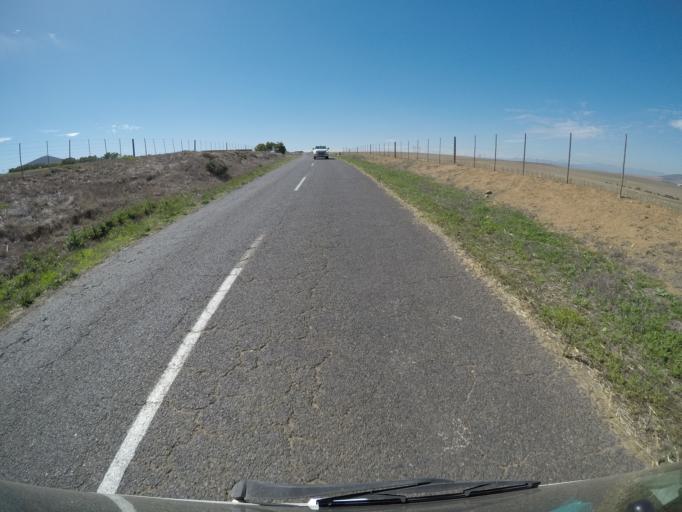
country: ZA
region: Western Cape
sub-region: City of Cape Town
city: Sunset Beach
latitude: -33.7420
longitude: 18.5622
